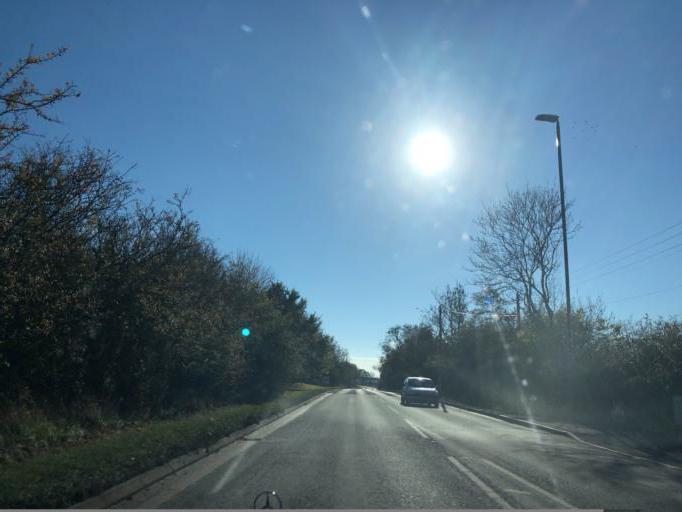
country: GB
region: England
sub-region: Warwickshire
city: Southam
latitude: 52.2449
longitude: -1.3916
